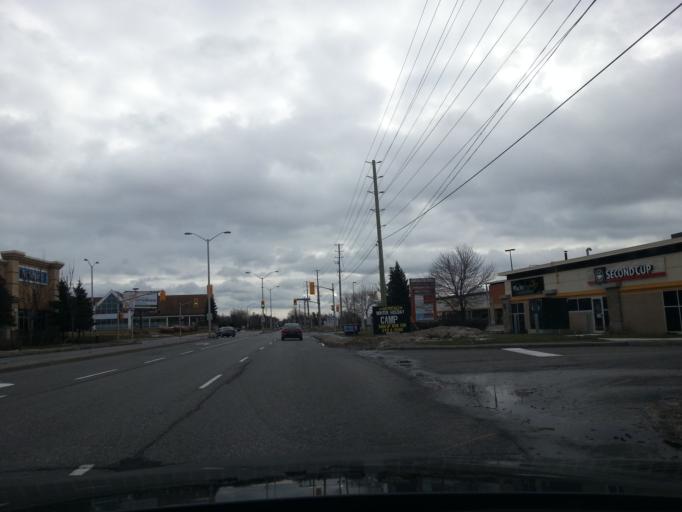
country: CA
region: Ontario
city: Bells Corners
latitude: 45.2696
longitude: -75.7460
